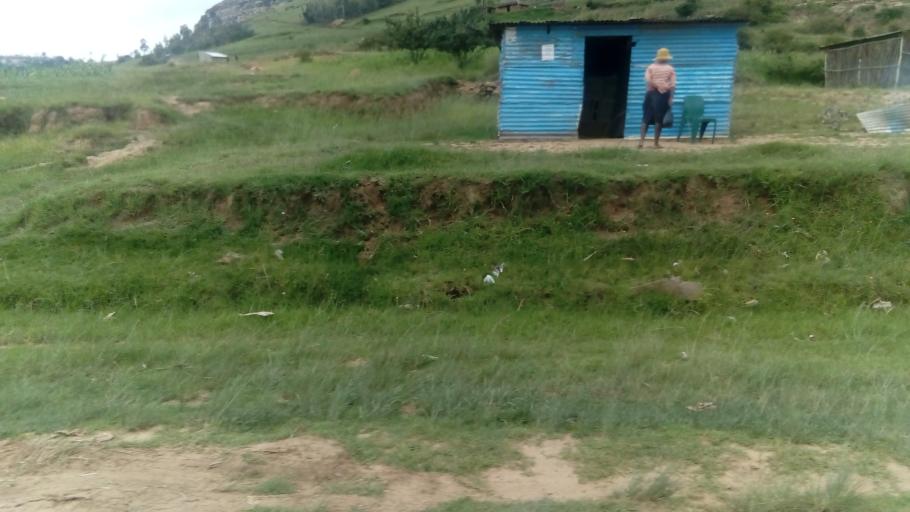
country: LS
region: Leribe
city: Leribe
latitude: -28.9632
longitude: 28.1716
